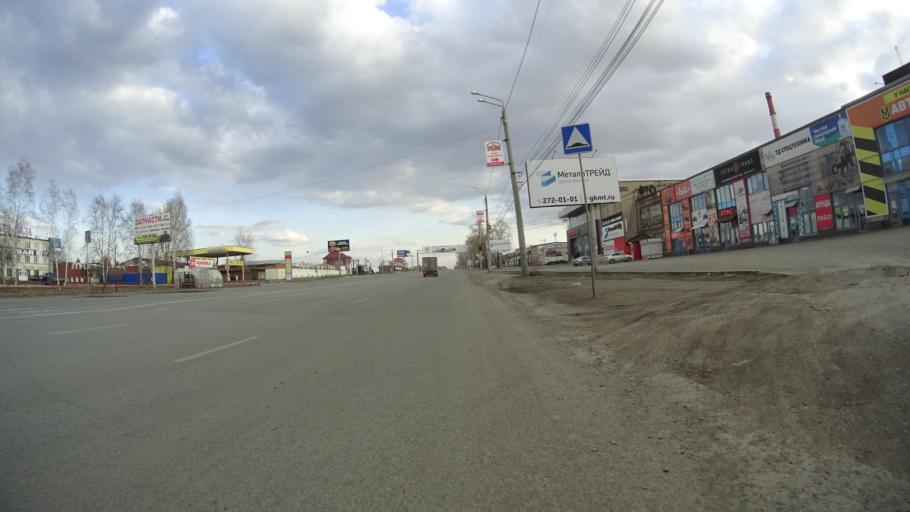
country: RU
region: Chelyabinsk
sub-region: Gorod Chelyabinsk
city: Chelyabinsk
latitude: 55.1121
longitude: 61.3866
